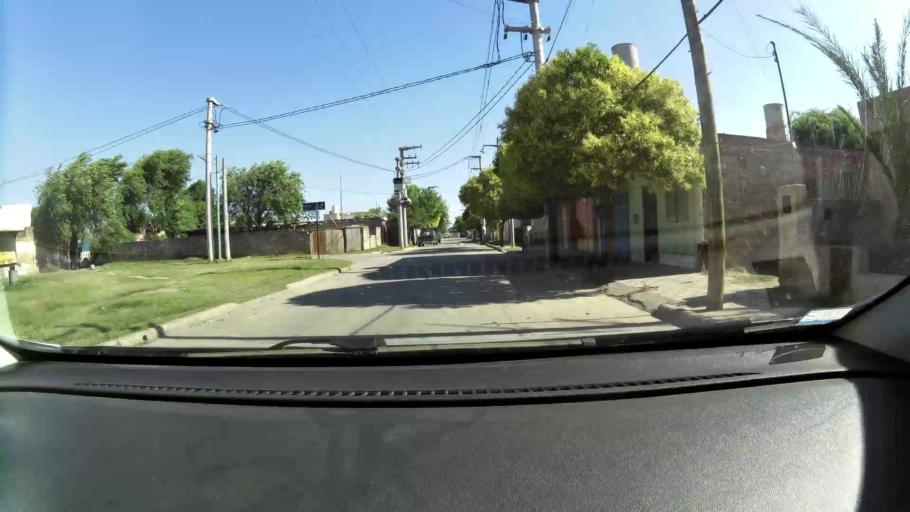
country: AR
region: Cordoba
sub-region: Departamento de Capital
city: Cordoba
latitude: -31.3734
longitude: -64.1870
